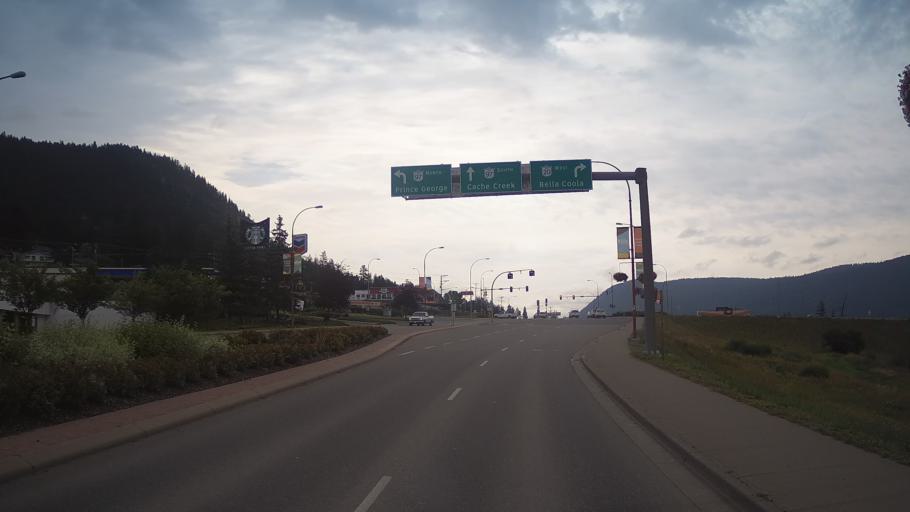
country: CA
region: British Columbia
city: Williams Lake
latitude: 52.1280
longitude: -122.1307
